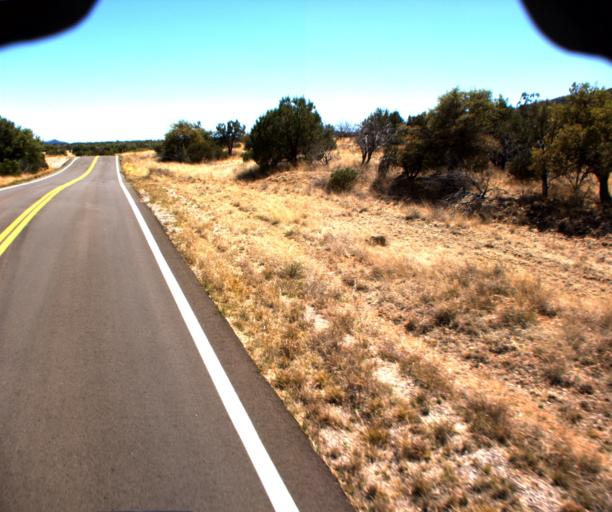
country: US
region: Arizona
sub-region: Cochise County
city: Huachuca City
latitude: 31.5630
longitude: -110.5550
